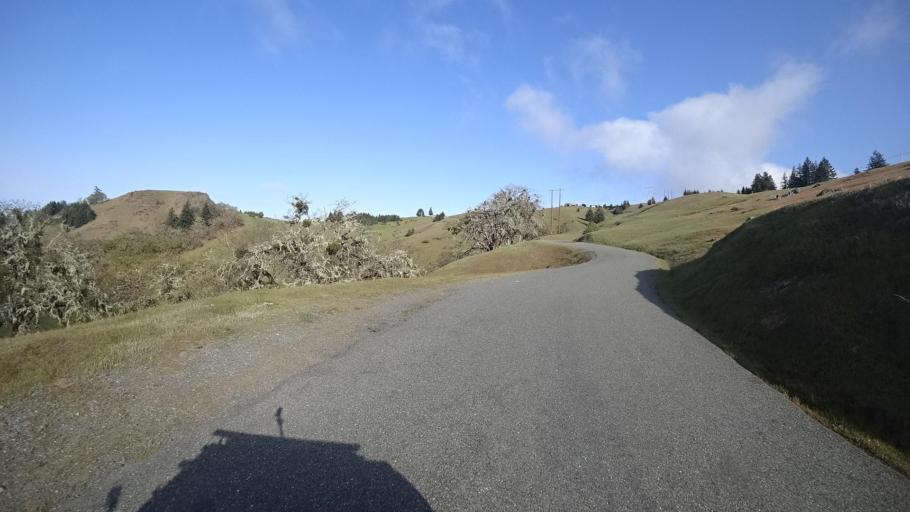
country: US
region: California
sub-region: Humboldt County
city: Blue Lake
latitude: 40.7189
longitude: -123.9428
